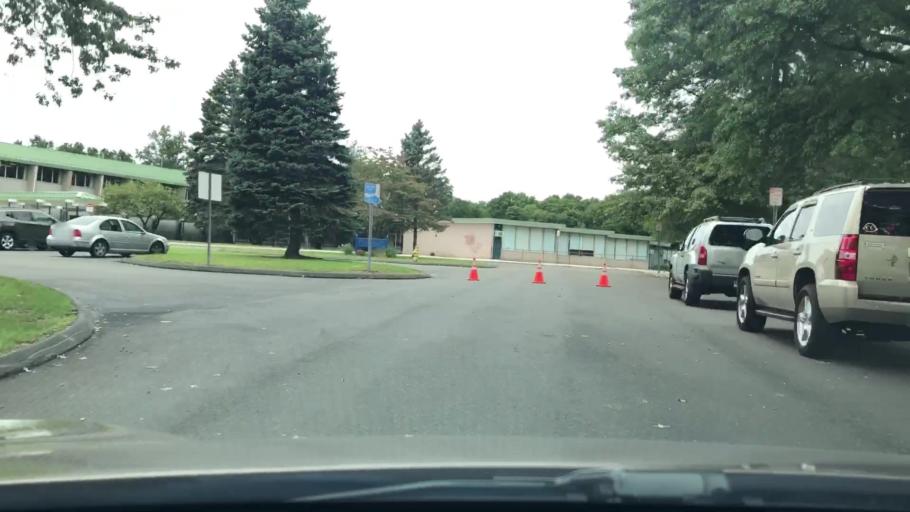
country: US
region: Connecticut
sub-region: Fairfield County
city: Darien
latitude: 41.1156
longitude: -73.4533
